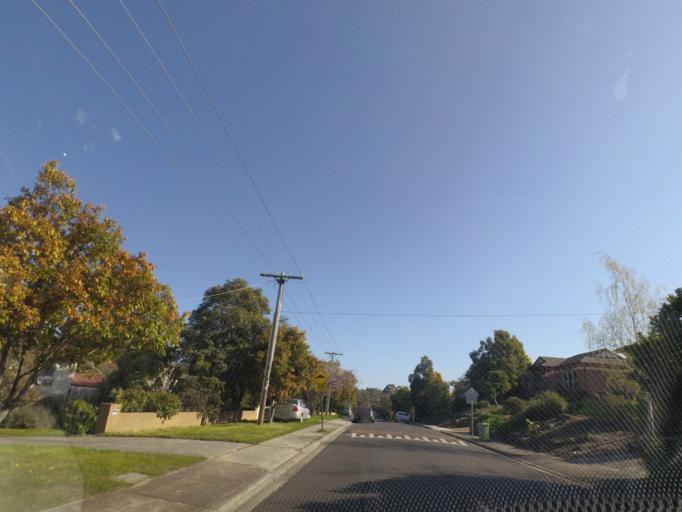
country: AU
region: Victoria
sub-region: Whitehorse
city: Mont Albert North
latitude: -37.7943
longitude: 145.1065
